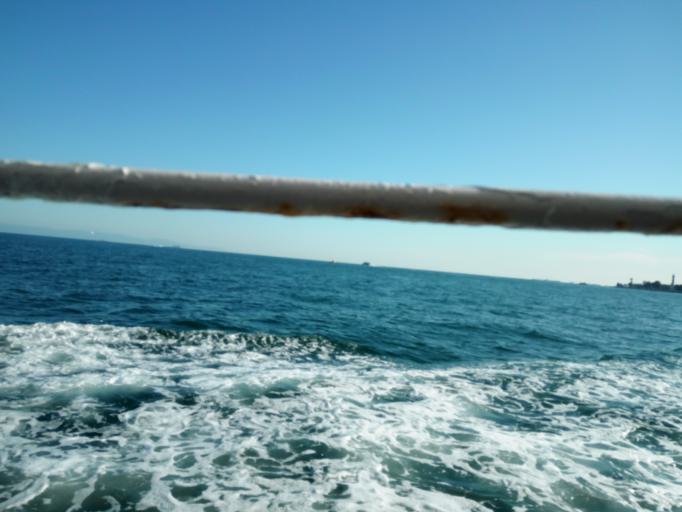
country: TR
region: Istanbul
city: Eminoenue
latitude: 41.0128
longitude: 28.9985
